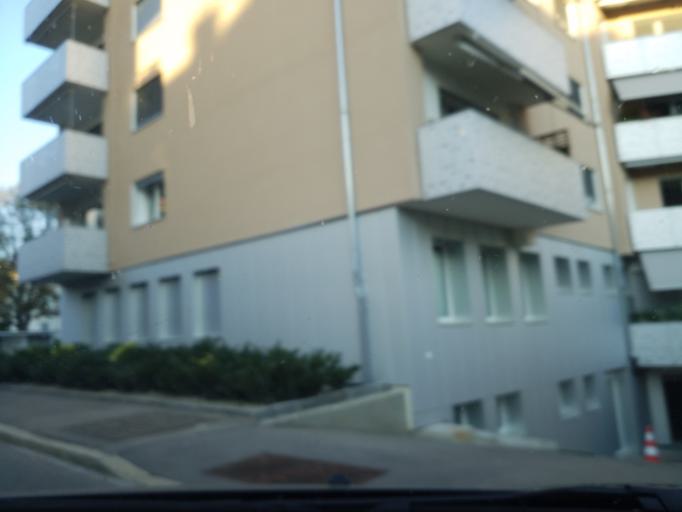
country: CH
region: Vaud
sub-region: Riviera-Pays-d'Enhaut District
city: Vevey
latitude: 46.4592
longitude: 6.8499
